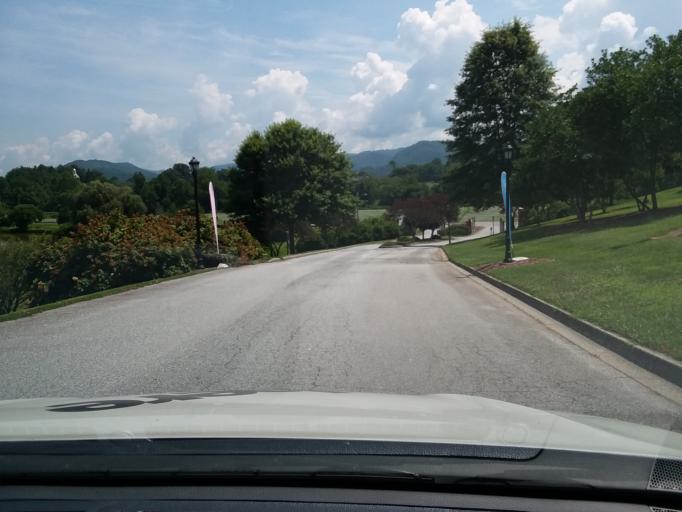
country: US
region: Georgia
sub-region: Rabun County
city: Mountain City
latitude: 34.9623
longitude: -83.3899
